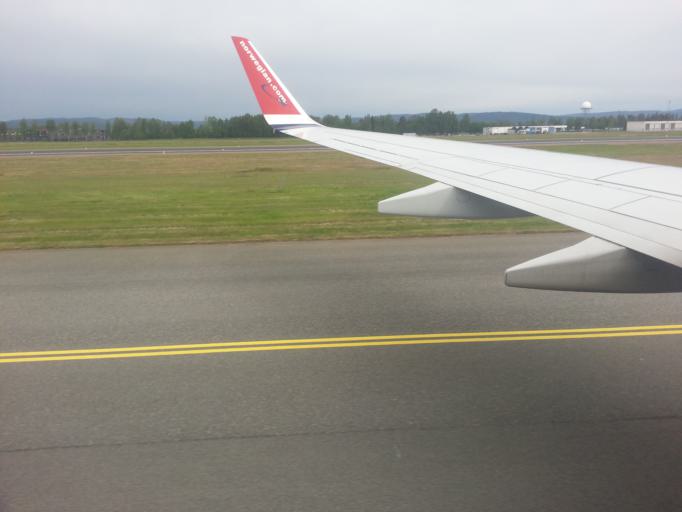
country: NO
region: Akershus
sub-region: Nannestad
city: Teigebyen
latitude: 60.1940
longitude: 11.0829
